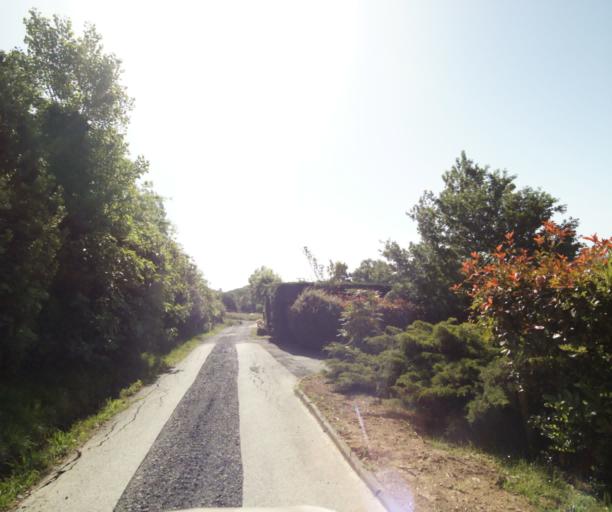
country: FR
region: Aquitaine
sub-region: Departement des Pyrenees-Atlantiques
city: Villefranque
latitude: 43.4525
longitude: -1.4434
